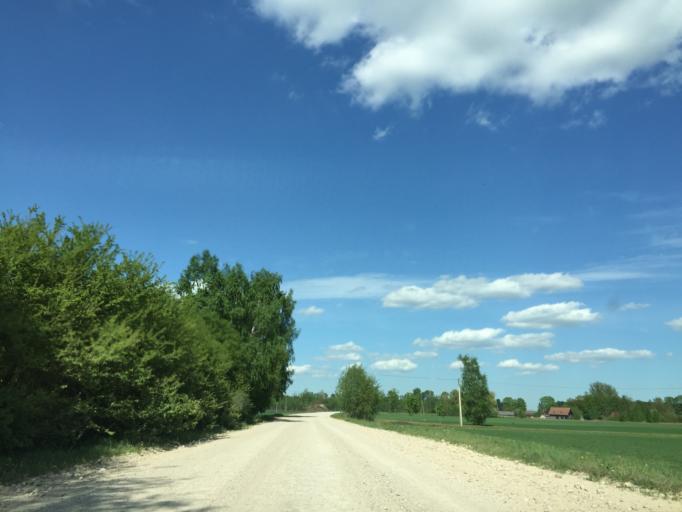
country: LV
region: Rundales
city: Pilsrundale
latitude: 56.3884
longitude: 24.0913
